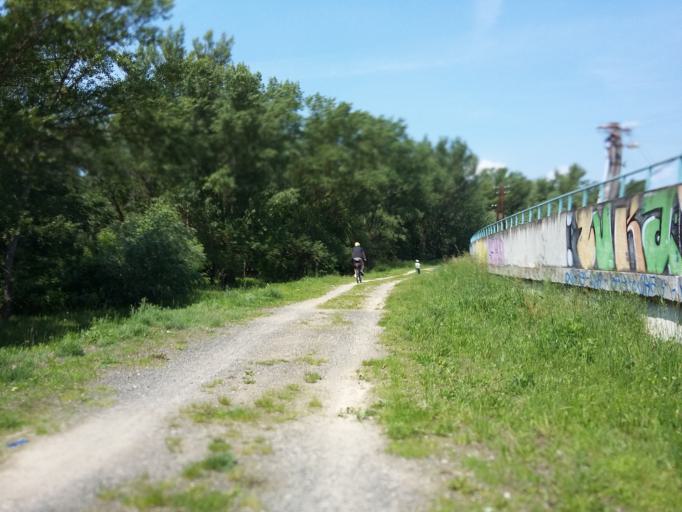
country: AT
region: Lower Austria
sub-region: Politischer Bezirk Ganserndorf
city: Angern an der March
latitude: 48.4053
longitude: 16.8540
